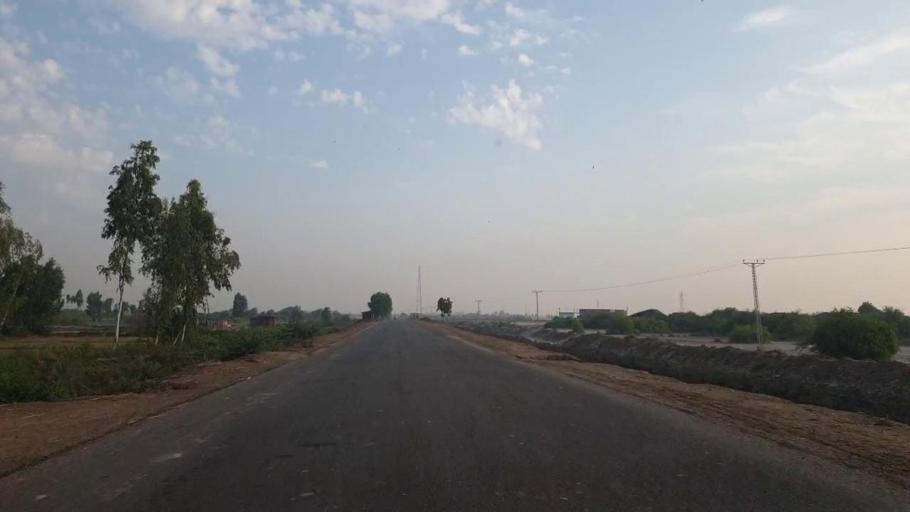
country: PK
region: Sindh
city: Badin
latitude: 24.6929
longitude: 68.9178
